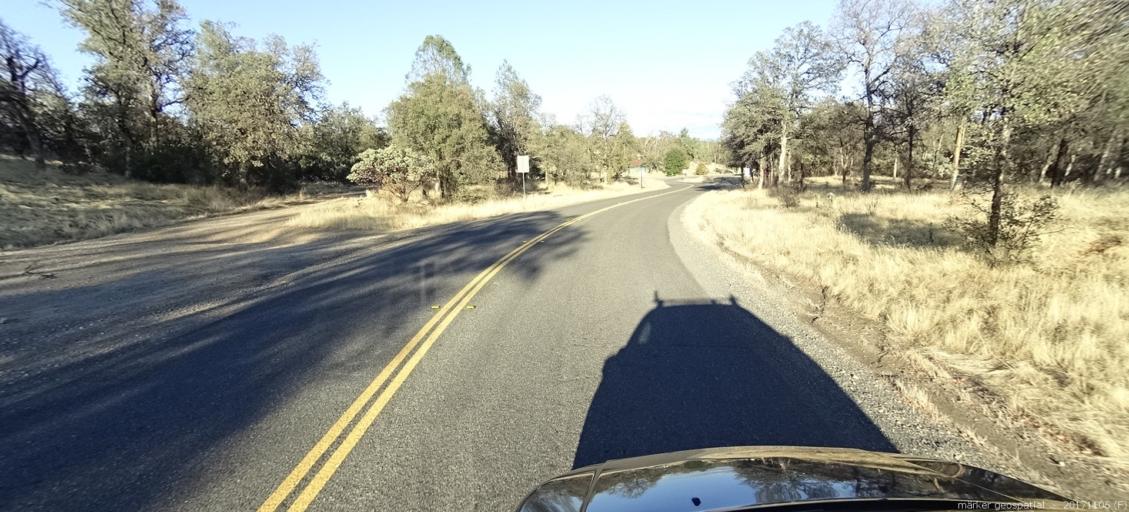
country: US
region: California
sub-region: Shasta County
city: Shasta
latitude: 40.5836
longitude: -122.4478
